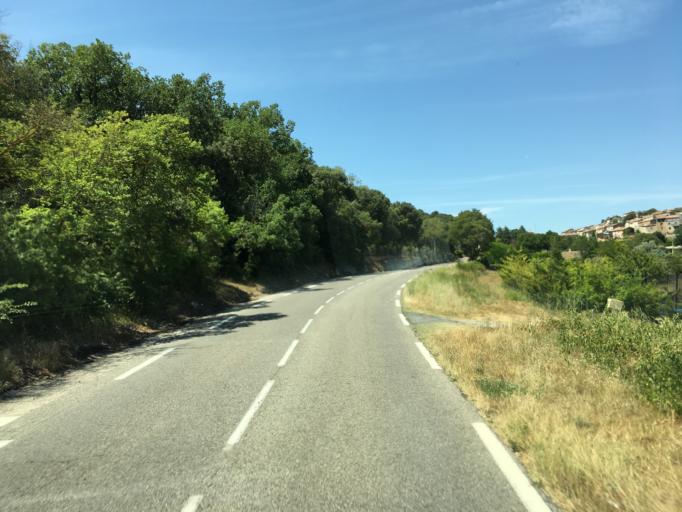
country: FR
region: Provence-Alpes-Cote d'Azur
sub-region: Departement du Var
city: Ginasservis
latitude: 43.6658
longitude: 5.8517
